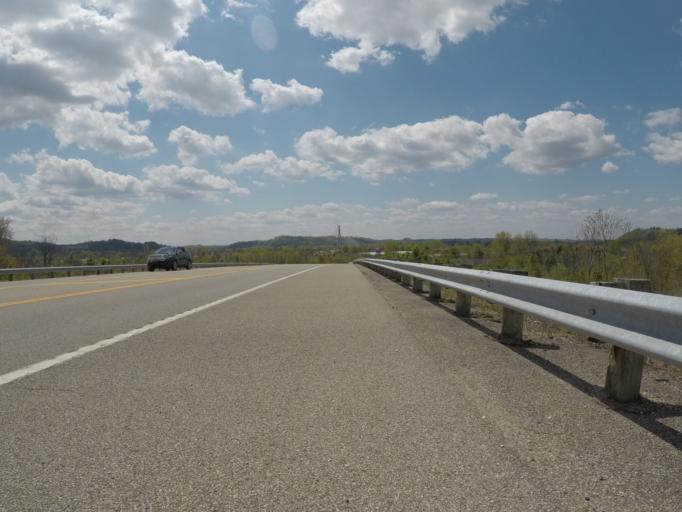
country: US
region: West Virginia
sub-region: Cabell County
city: Pea Ridge
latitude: 38.4470
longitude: -82.3793
